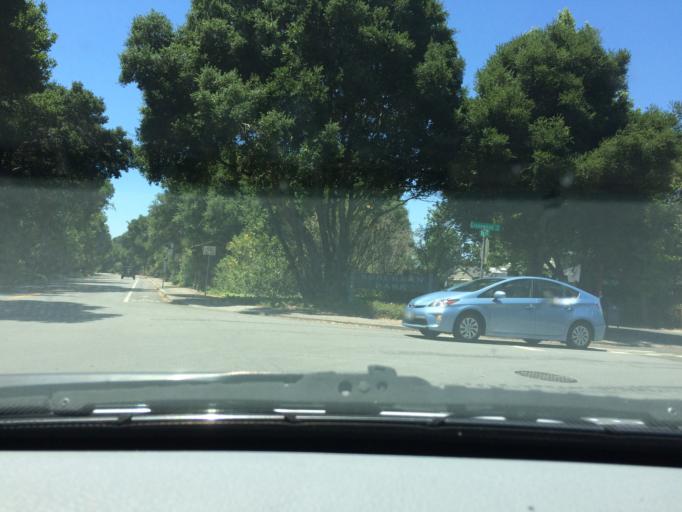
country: US
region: California
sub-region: San Mateo County
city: North Fair Oaks
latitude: 37.4755
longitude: -122.1752
